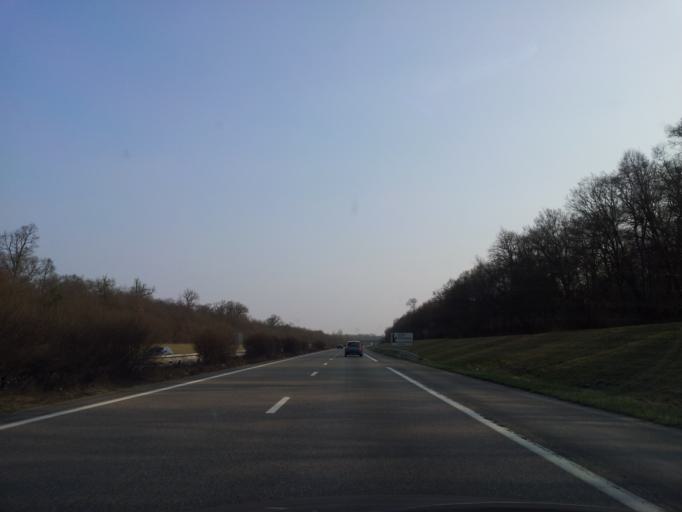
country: FR
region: Alsace
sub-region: Departement du Haut-Rhin
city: Bartenheim
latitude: 47.6584
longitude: 7.4856
